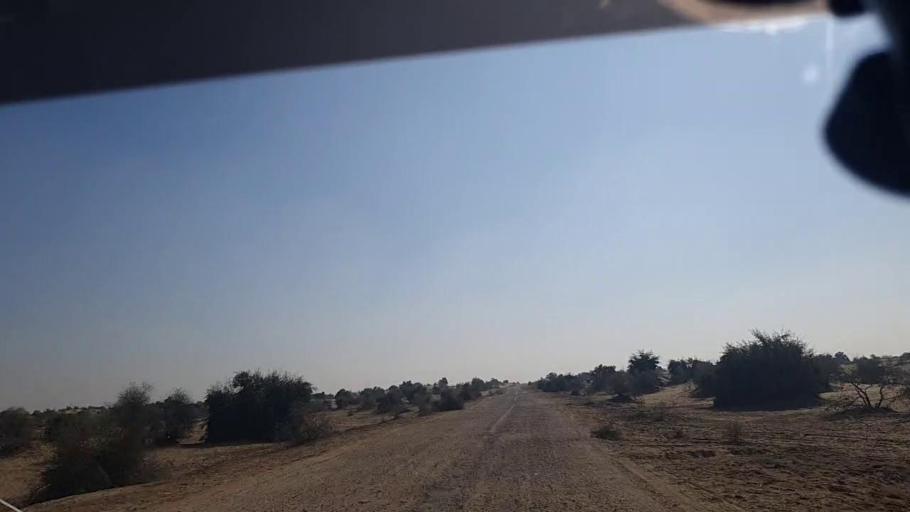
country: PK
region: Sindh
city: Khanpur
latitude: 27.5782
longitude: 69.3054
